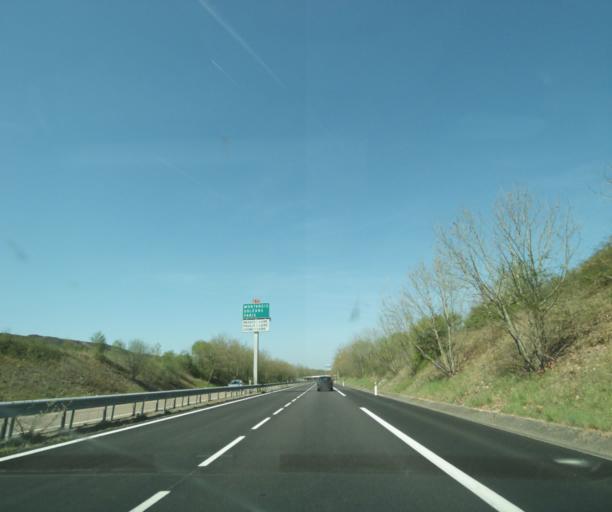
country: FR
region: Bourgogne
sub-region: Departement de la Nievre
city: La Charite-sur-Loire
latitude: 47.1999
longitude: 3.0183
